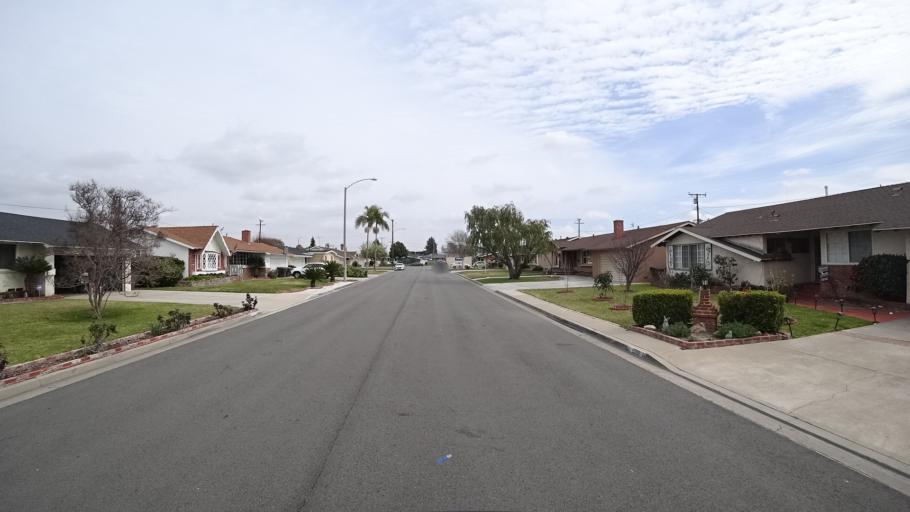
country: US
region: California
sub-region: Orange County
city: Stanton
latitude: 33.8201
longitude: -117.9882
